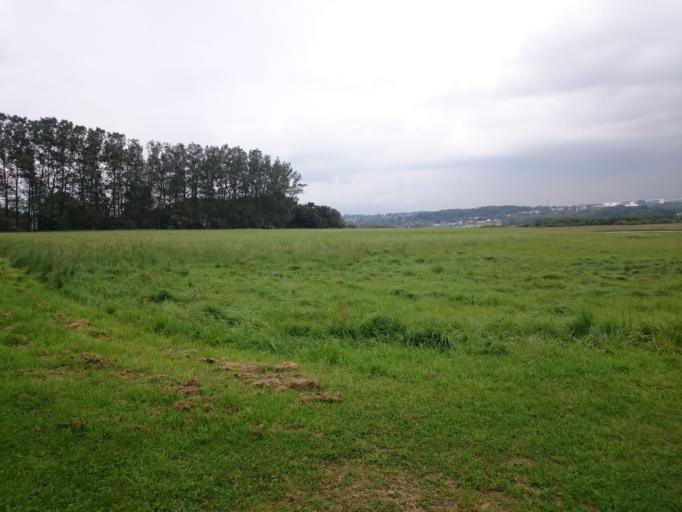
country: DK
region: Central Jutland
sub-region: Arhus Kommune
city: Stavtrup
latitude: 56.1365
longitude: 10.1276
